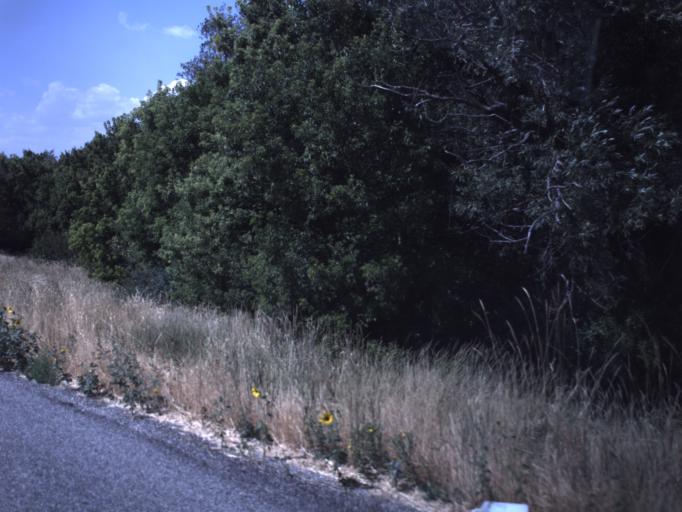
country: US
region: Utah
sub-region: Cache County
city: Mendon
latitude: 41.7958
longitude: -112.0422
